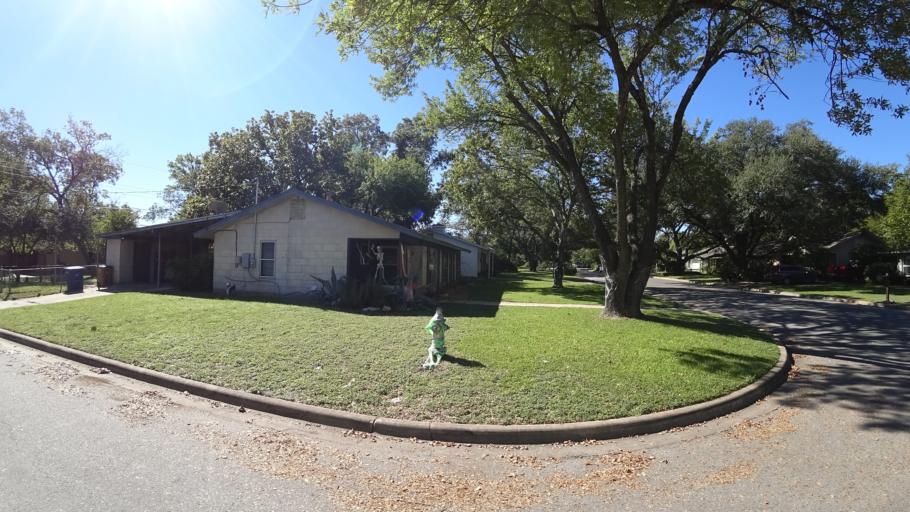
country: US
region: Texas
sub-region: Travis County
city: Austin
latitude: 30.3048
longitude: -97.6887
